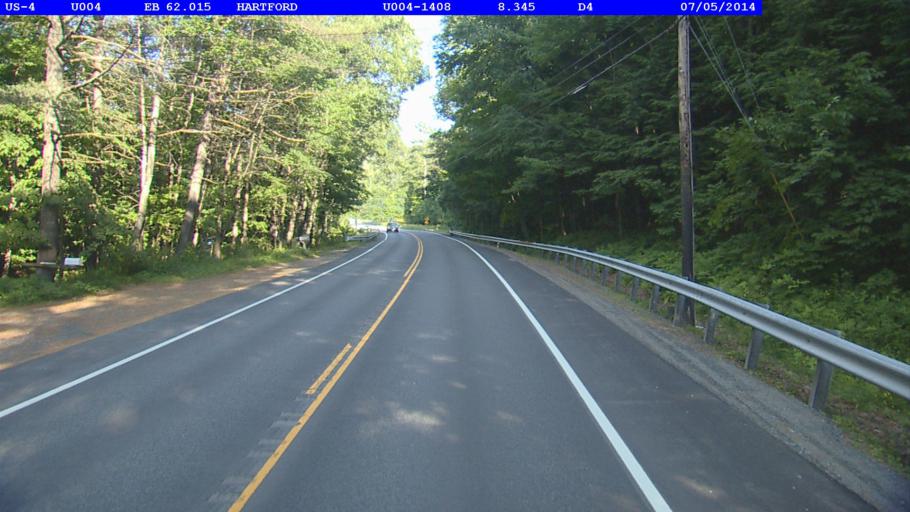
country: US
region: Vermont
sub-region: Windsor County
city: White River Junction
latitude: 43.6581
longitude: -72.3469
